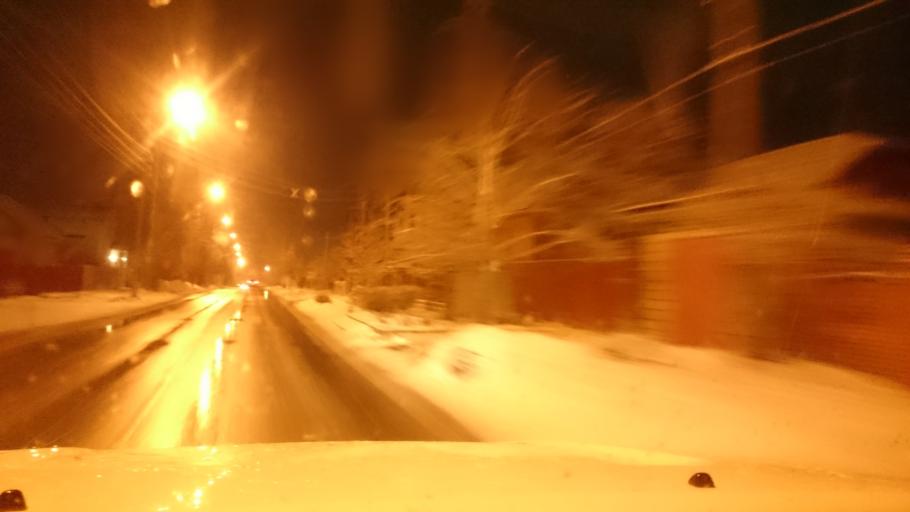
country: RU
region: Tula
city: Tula
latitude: 54.2037
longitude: 37.5548
